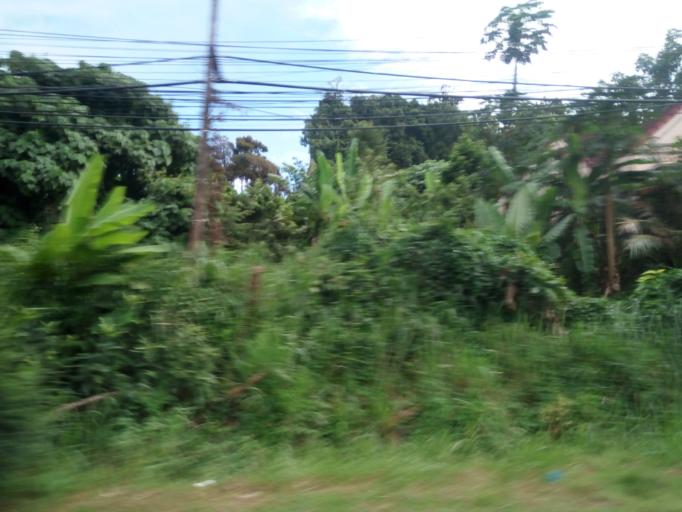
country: TH
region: Phuket
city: Mueang Phuket
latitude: 7.8440
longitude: 98.3889
